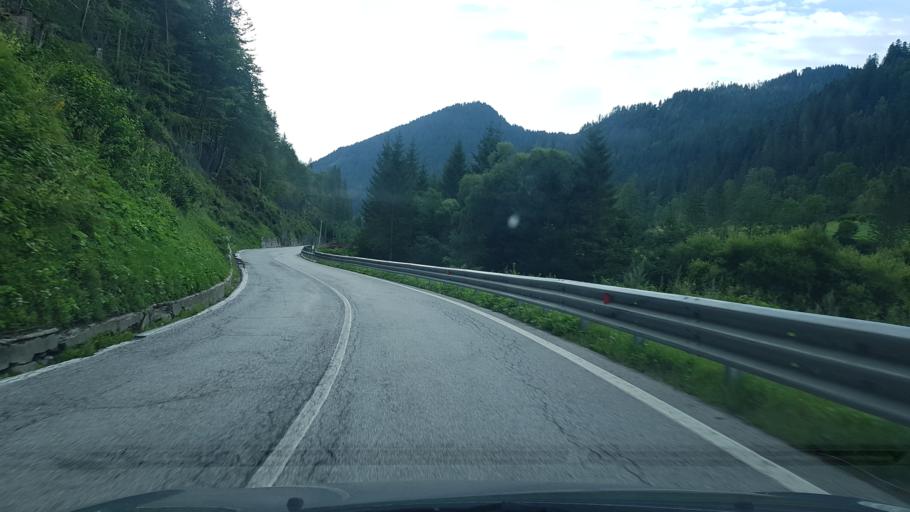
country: IT
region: Friuli Venezia Giulia
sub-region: Provincia di Udine
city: Forni Avoltri
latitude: 46.5760
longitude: 12.7943
